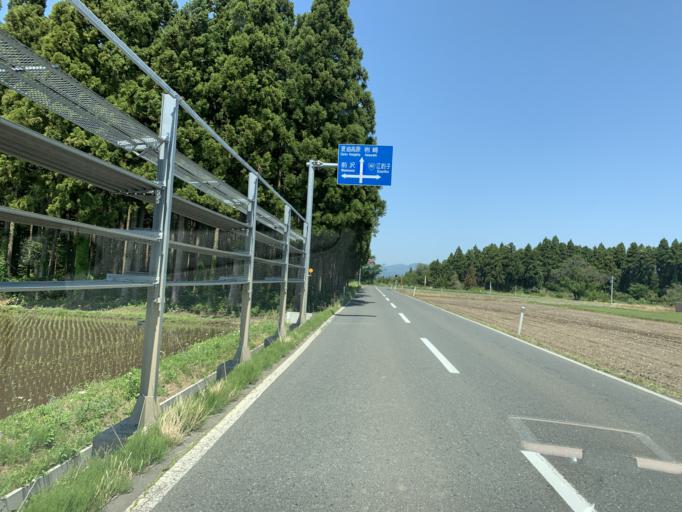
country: JP
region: Iwate
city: Kitakami
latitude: 39.2751
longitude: 141.0515
